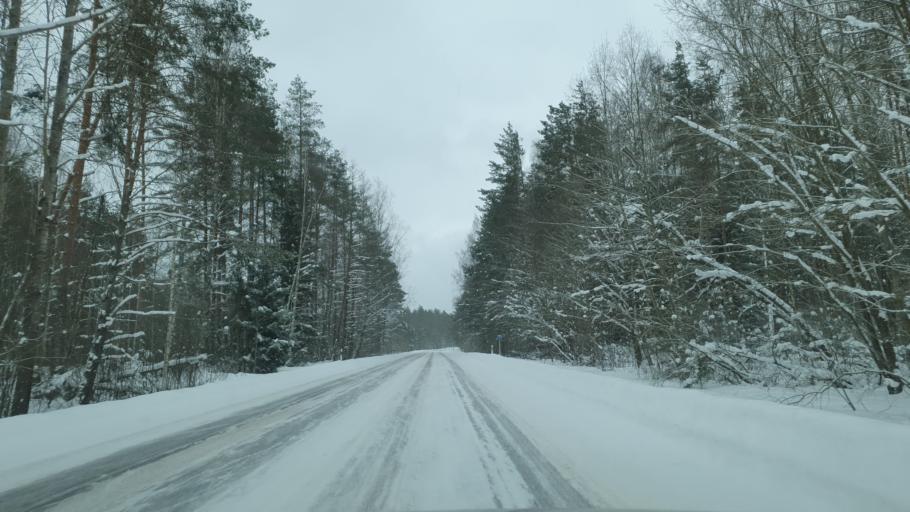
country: EE
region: Polvamaa
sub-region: Raepina vald
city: Rapina
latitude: 57.9951
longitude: 27.5554
